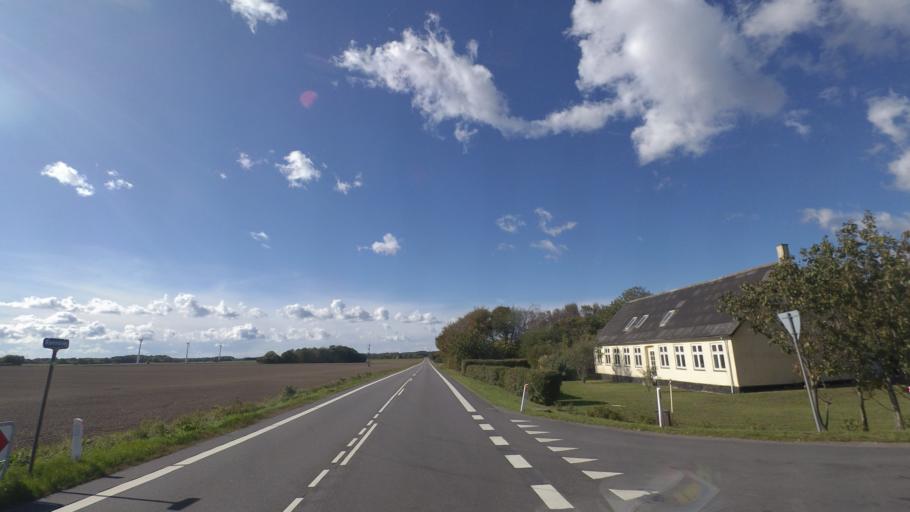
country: DK
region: Capital Region
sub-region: Bornholm Kommune
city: Nexo
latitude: 55.0612
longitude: 15.0669
